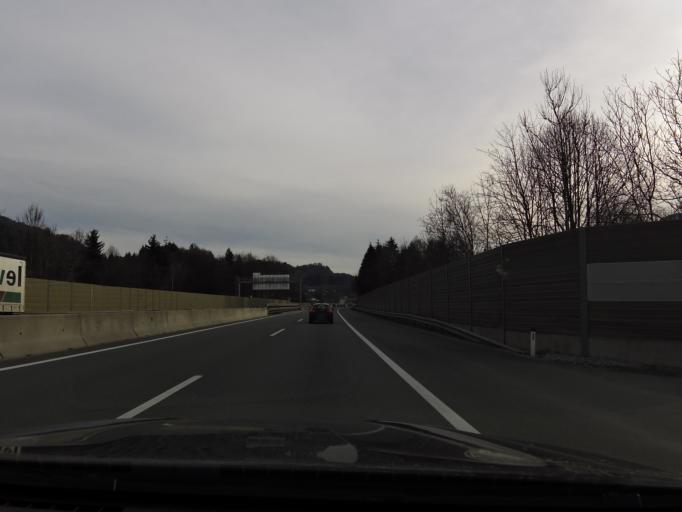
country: AT
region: Tyrol
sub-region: Politischer Bezirk Kufstein
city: Kufstein
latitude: 47.5797
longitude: 12.1498
